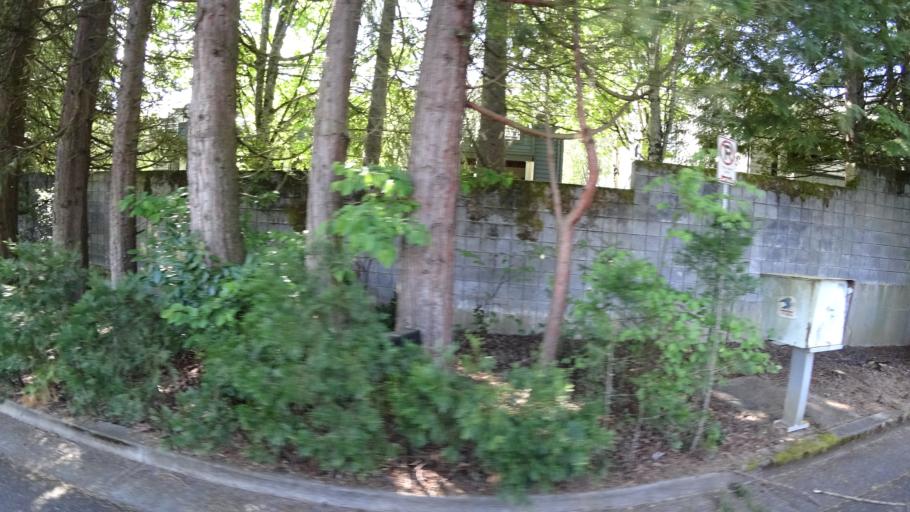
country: US
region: Oregon
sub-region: Washington County
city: King City
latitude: 45.4432
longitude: -122.8219
